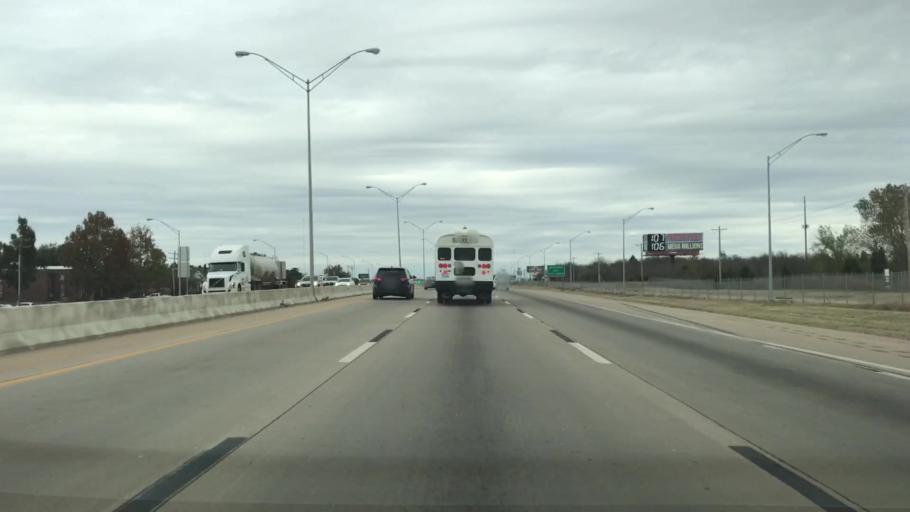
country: US
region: Oklahoma
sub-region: Cleveland County
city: Moore
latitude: 35.3687
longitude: -97.4948
